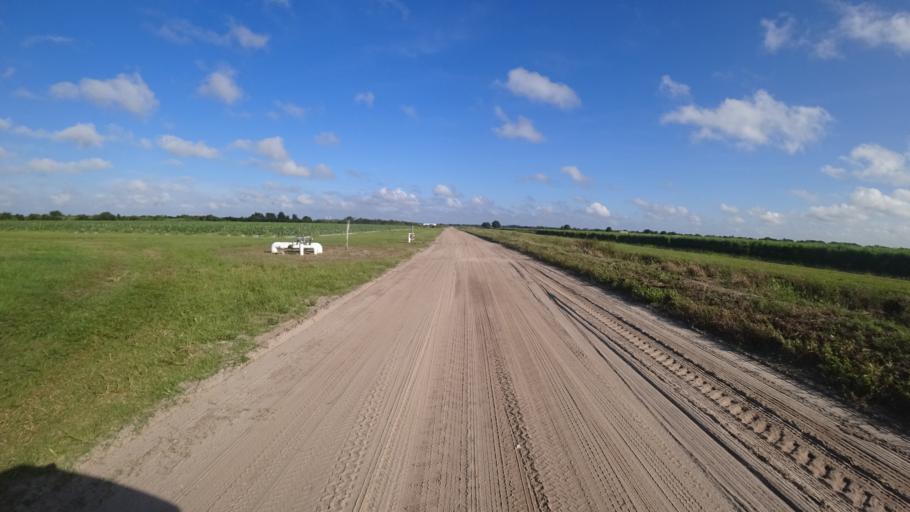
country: US
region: Florida
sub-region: Hillsborough County
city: Wimauma
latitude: 27.5346
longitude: -82.3179
